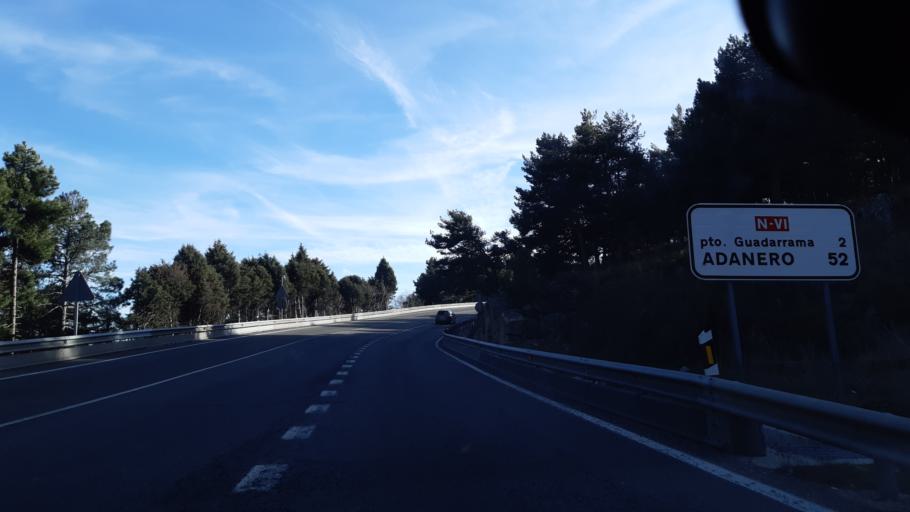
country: ES
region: Madrid
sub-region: Provincia de Madrid
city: Guadarrama
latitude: 40.7087
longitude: -4.1288
